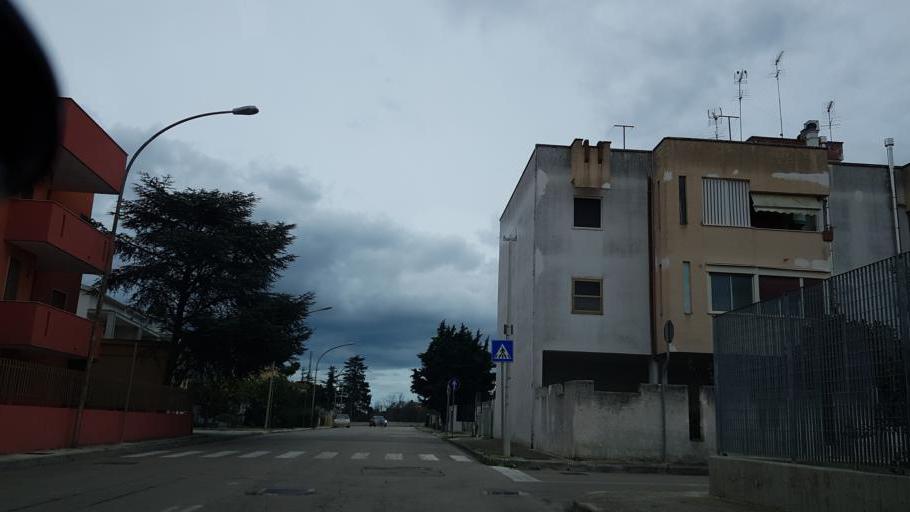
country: IT
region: Apulia
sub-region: Provincia di Brindisi
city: La Rosa
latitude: 40.6083
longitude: 17.9517
